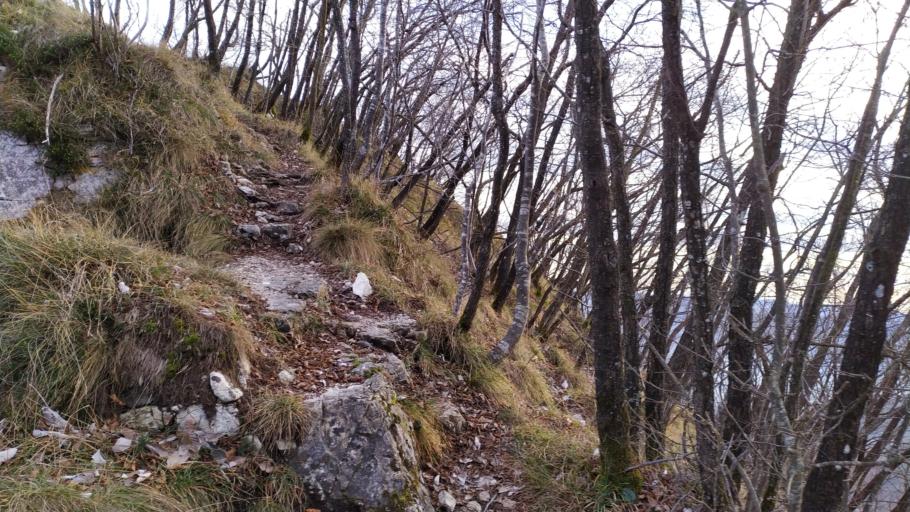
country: IT
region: Veneto
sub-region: Provincia di Vicenza
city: Velo d'Astico
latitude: 45.7669
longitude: 11.3716
